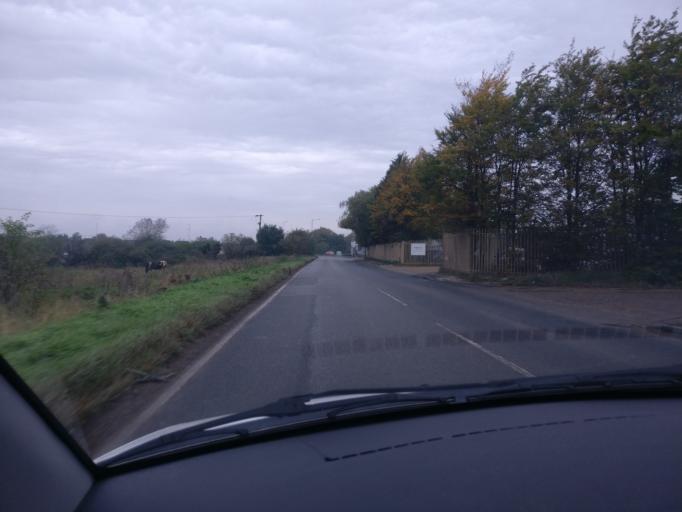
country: GB
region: England
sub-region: Peterborough
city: Eye
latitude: 52.5887
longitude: -0.2010
